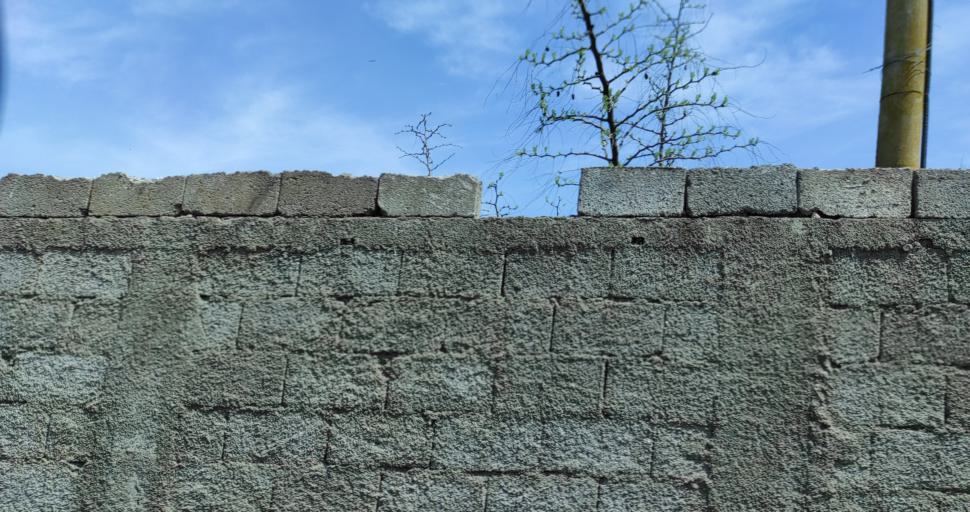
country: AL
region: Shkoder
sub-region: Rrethi i Malesia e Madhe
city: Gruemire
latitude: 42.1375
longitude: 19.5466
